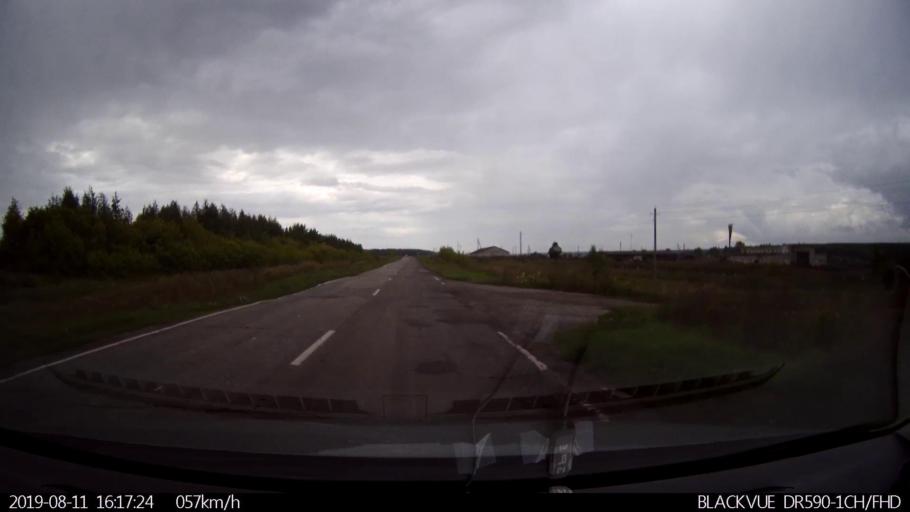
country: RU
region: Ulyanovsk
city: Mayna
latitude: 54.0483
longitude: 47.6163
